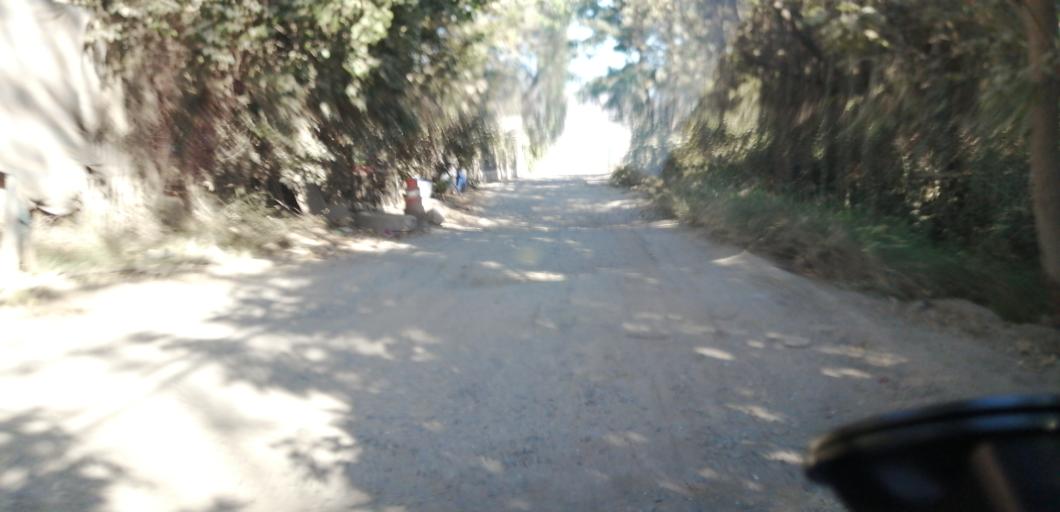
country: CL
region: Santiago Metropolitan
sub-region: Provincia de Santiago
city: Lo Prado
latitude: -33.4630
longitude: -70.7763
